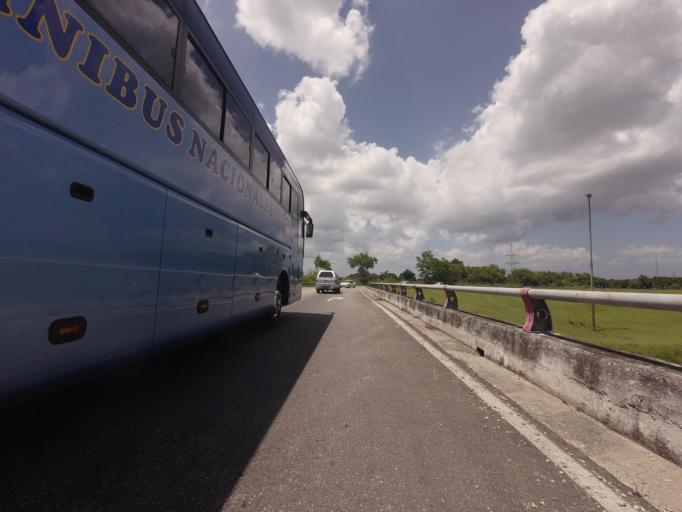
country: CU
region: La Habana
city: Arroyo Naranjo
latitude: 23.0700
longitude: -82.4006
